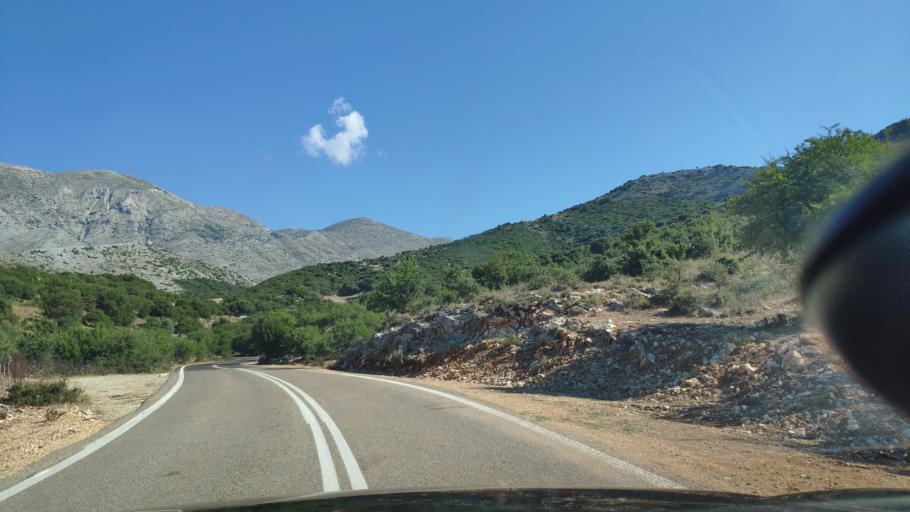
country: GR
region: West Greece
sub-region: Nomos Aitolias kai Akarnanias
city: Archontochorion
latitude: 38.6929
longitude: 21.0599
